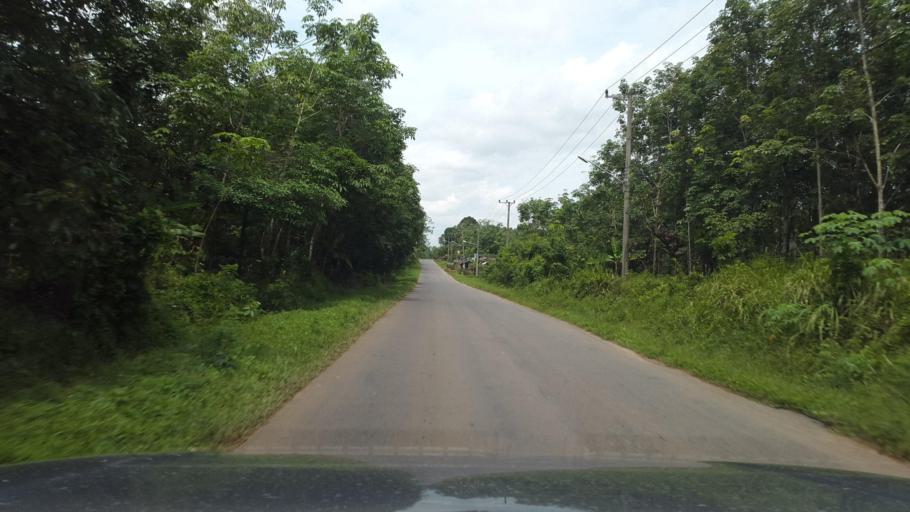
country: ID
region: South Sumatra
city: Gunungmegang Dalam
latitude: -3.3640
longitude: 103.9377
